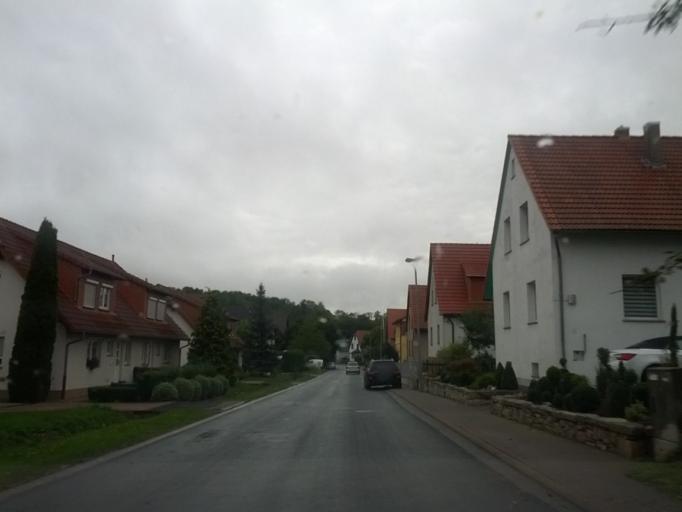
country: DE
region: Thuringia
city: Mechterstadt
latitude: 50.9406
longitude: 10.4841
